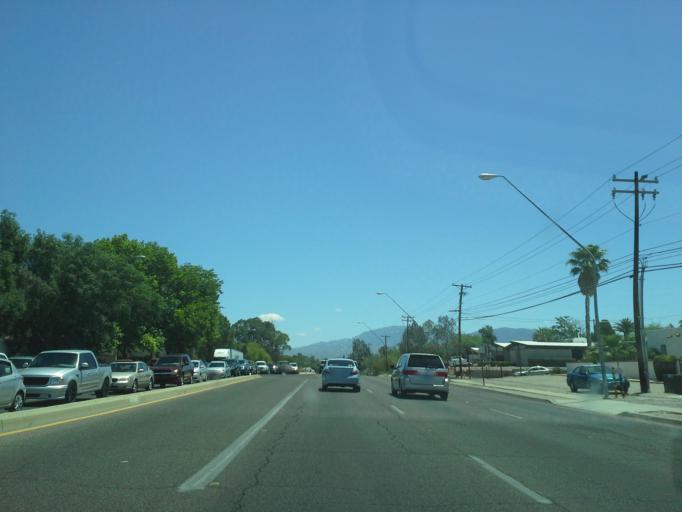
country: US
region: Arizona
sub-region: Pima County
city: Tucson
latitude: 32.2507
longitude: -110.8648
